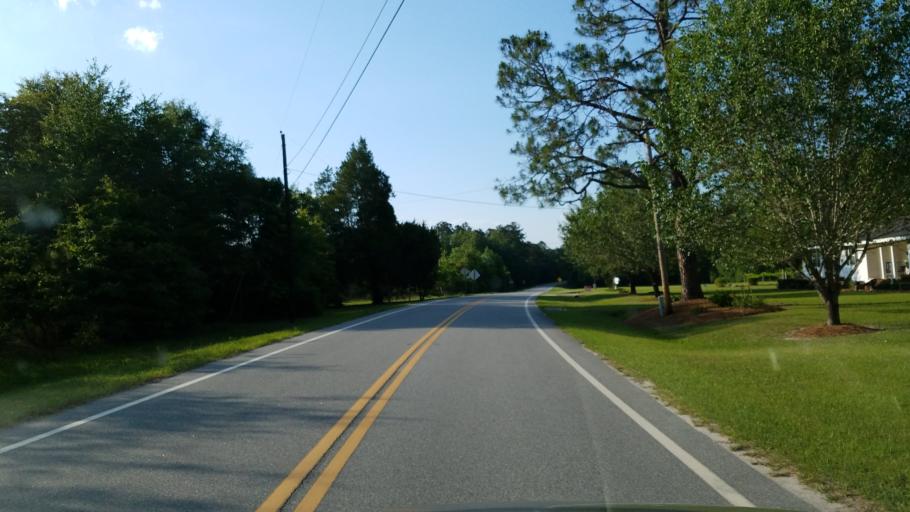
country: US
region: Georgia
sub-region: Echols County
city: Statenville
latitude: 30.8307
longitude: -83.0545
